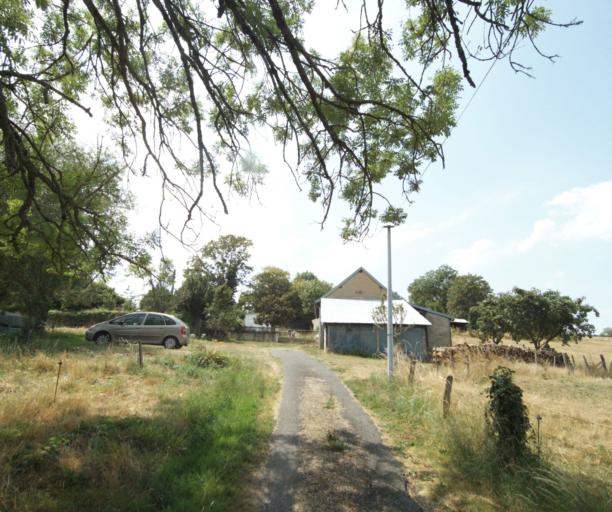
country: FR
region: Bourgogne
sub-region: Departement de Saone-et-Loire
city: Gueugnon
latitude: 46.6083
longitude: 4.0189
